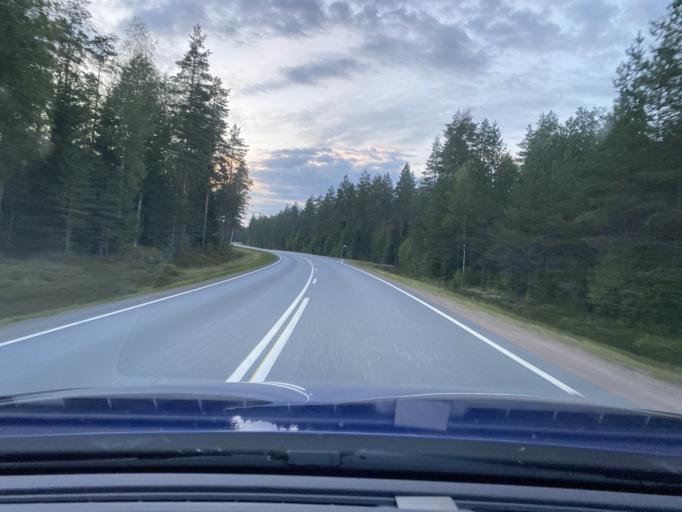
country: FI
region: Satakunta
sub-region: Pohjois-Satakunta
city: Honkajoki
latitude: 62.1213
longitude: 22.2488
